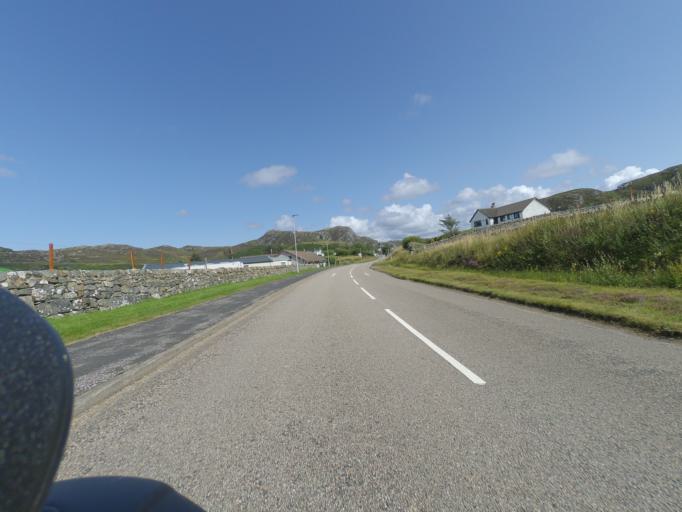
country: GB
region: Scotland
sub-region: Highland
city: Ullapool
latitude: 58.3511
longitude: -5.1566
